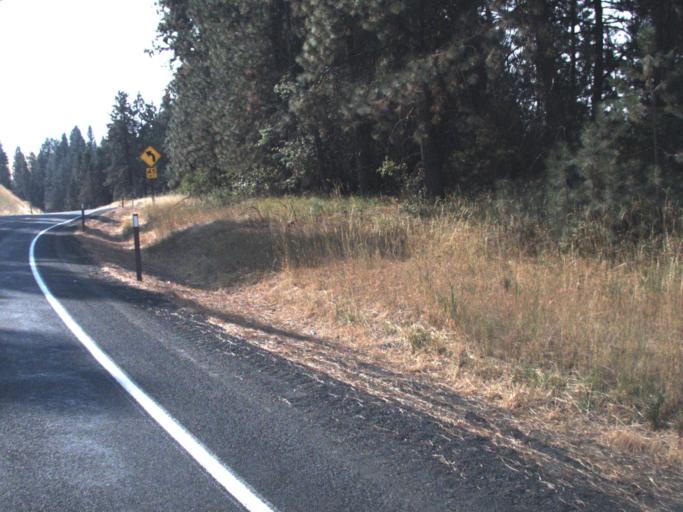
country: US
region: Washington
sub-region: Whitman County
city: Pullman
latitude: 46.9656
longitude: -117.1092
